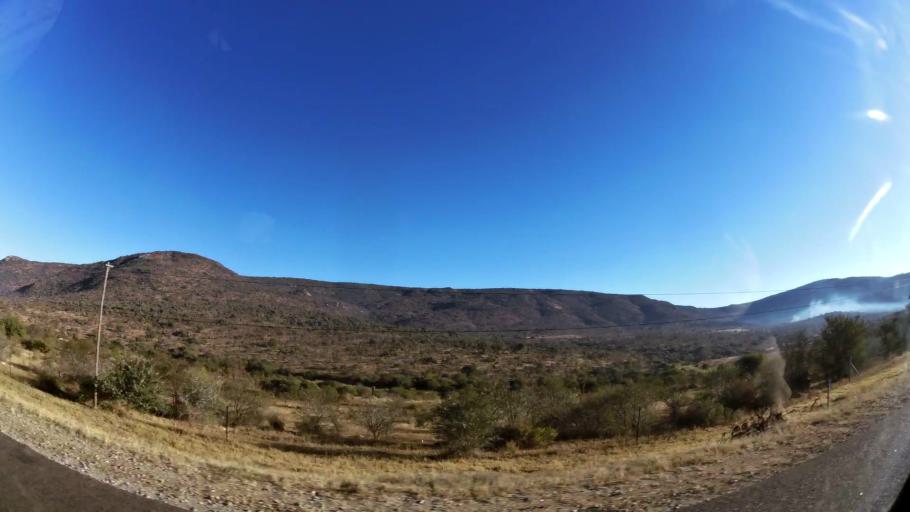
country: ZA
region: Limpopo
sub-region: Capricorn District Municipality
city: Mankoeng
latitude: -23.9385
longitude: 29.8290
